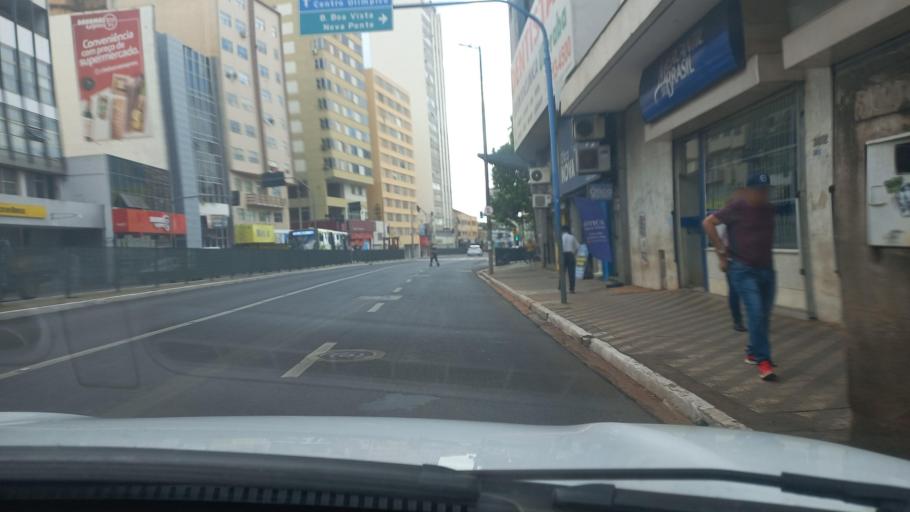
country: BR
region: Minas Gerais
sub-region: Uberaba
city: Uberaba
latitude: -19.7484
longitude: -47.9355
